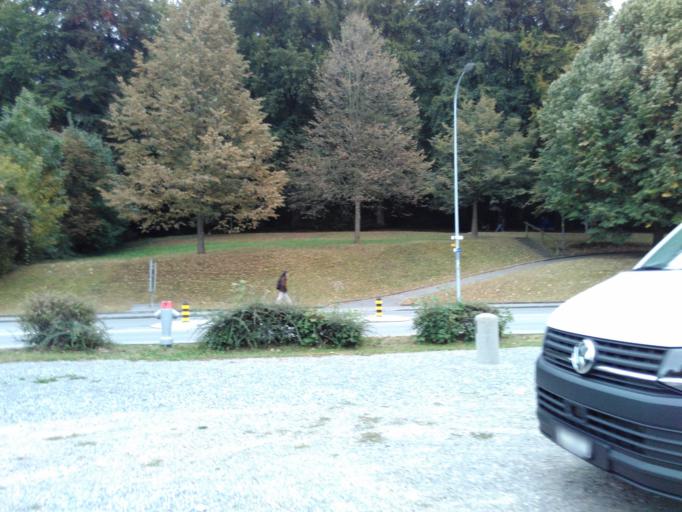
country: CH
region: Zurich
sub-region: Bezirk Buelach
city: Kloten / Holberg
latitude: 47.4465
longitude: 8.5819
